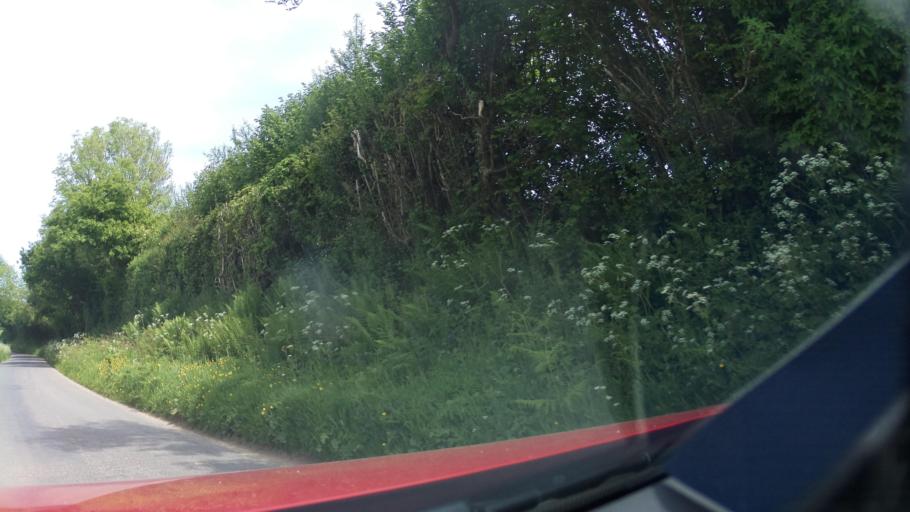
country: GB
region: England
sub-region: Devon
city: South Brent
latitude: 50.3684
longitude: -3.8040
